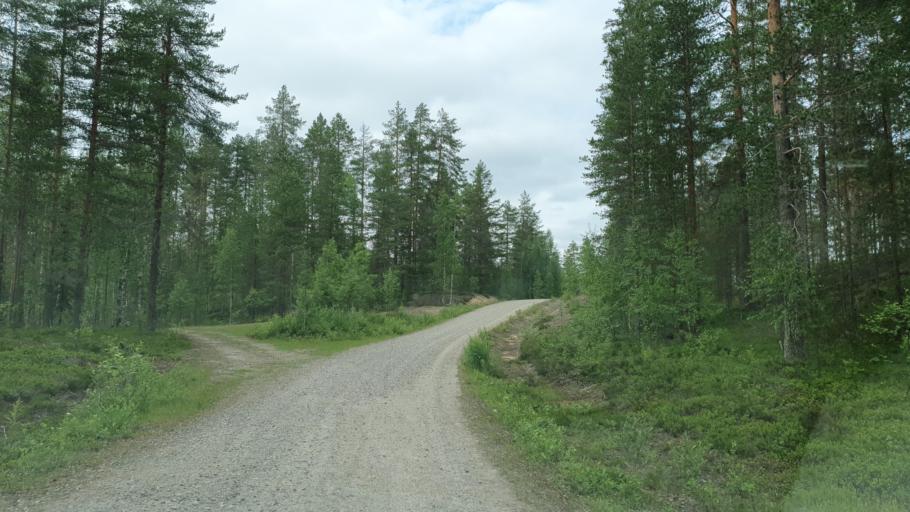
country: FI
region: Kainuu
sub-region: Kehys-Kainuu
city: Kuhmo
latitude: 63.9388
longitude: 29.5910
